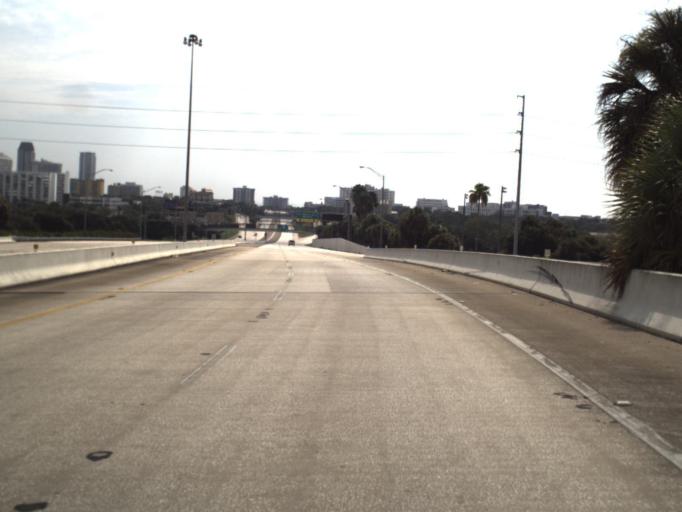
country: US
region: Florida
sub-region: Pinellas County
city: Saint Petersburg
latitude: 27.7660
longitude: -82.6561
